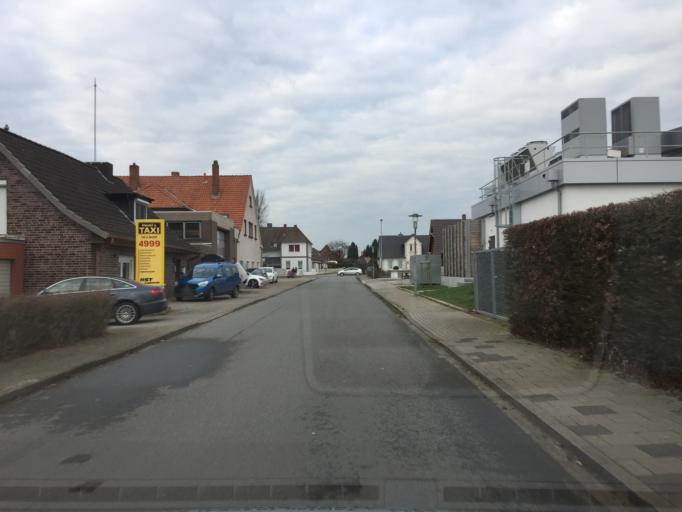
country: DE
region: Lower Saxony
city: Sulingen
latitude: 52.6824
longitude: 8.8214
